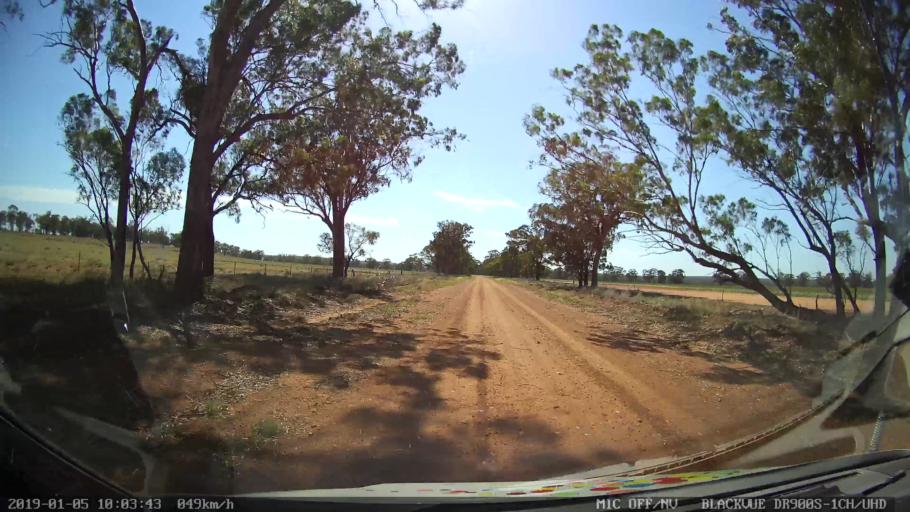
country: AU
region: New South Wales
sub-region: Gilgandra
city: Gilgandra
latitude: -31.6722
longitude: 148.8546
